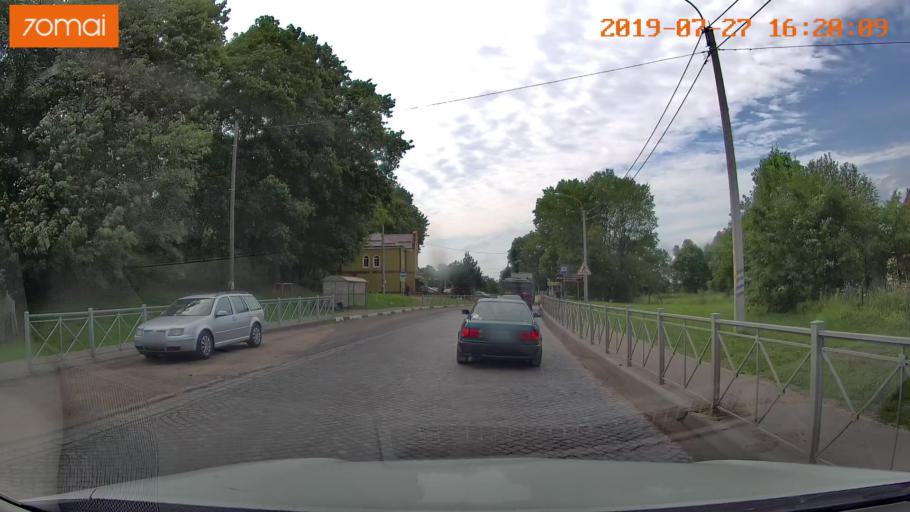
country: RU
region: Kaliningrad
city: Chernyakhovsk
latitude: 54.6260
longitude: 21.5264
